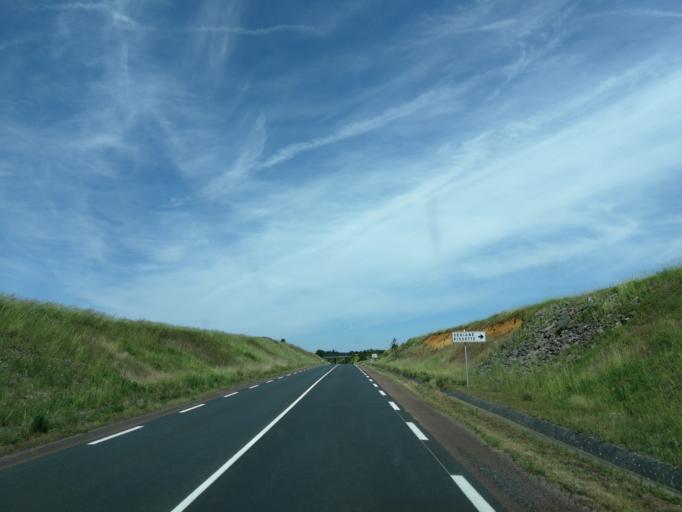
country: FR
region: Pays de la Loire
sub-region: Departement de la Vendee
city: Pissotte
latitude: 46.4982
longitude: -0.8249
